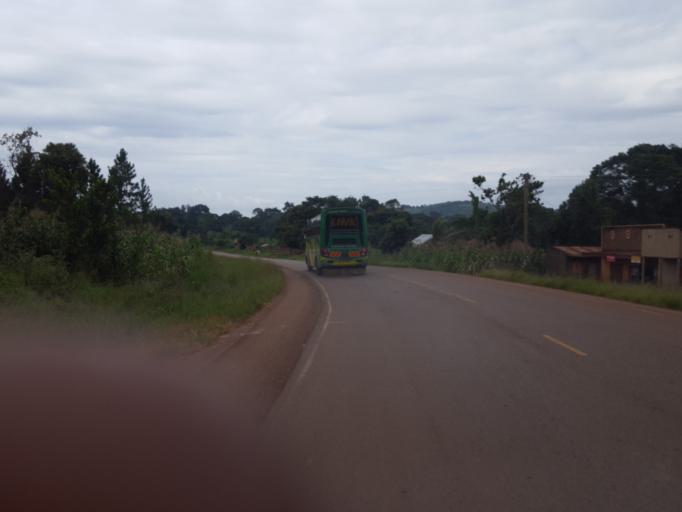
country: UG
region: Central Region
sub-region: Mityana District
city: Mityana
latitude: 0.6693
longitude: 32.0864
